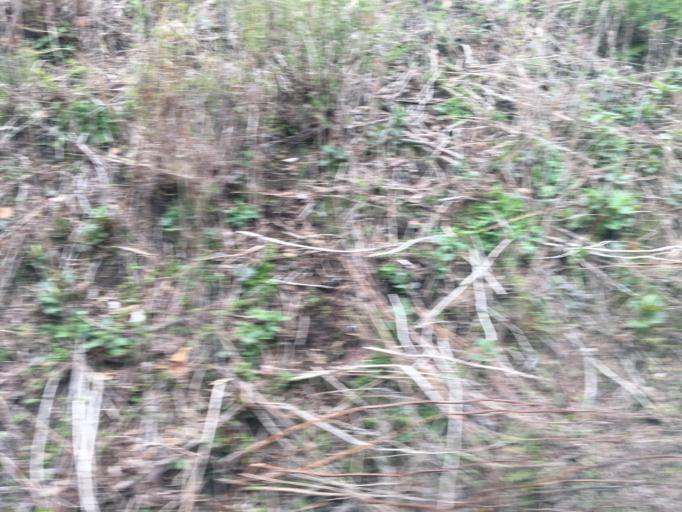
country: JP
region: Aomori
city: Shimokizukuri
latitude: 40.6660
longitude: 139.9405
